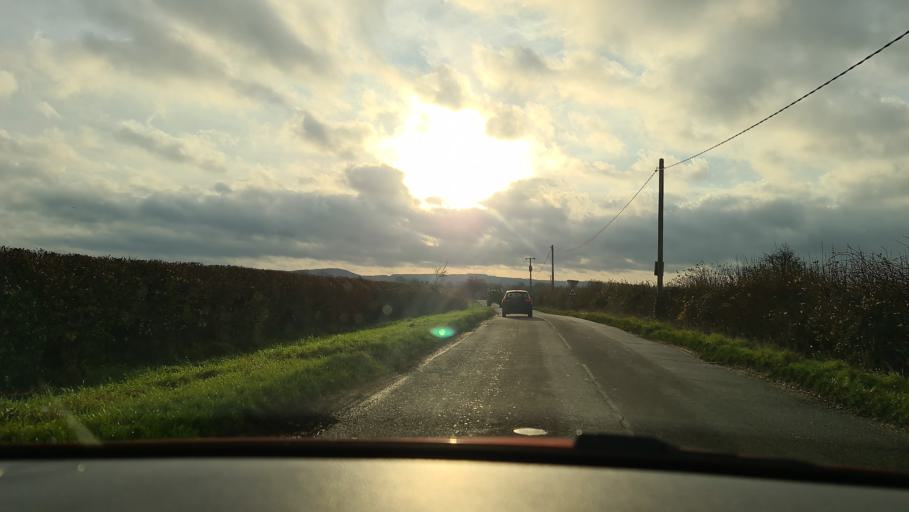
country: GB
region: England
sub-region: Buckinghamshire
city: Stone
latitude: 51.7828
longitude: -0.8810
